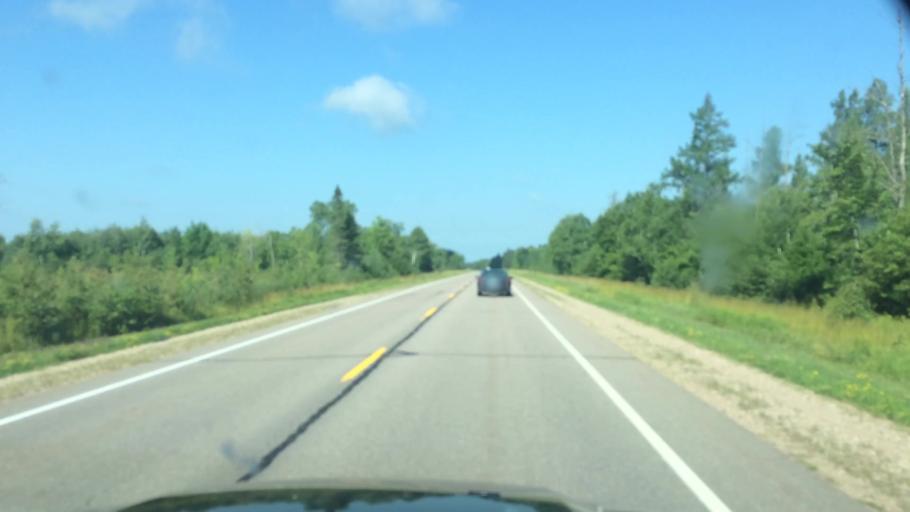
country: US
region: Wisconsin
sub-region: Langlade County
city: Antigo
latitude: 45.1452
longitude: -89.3158
